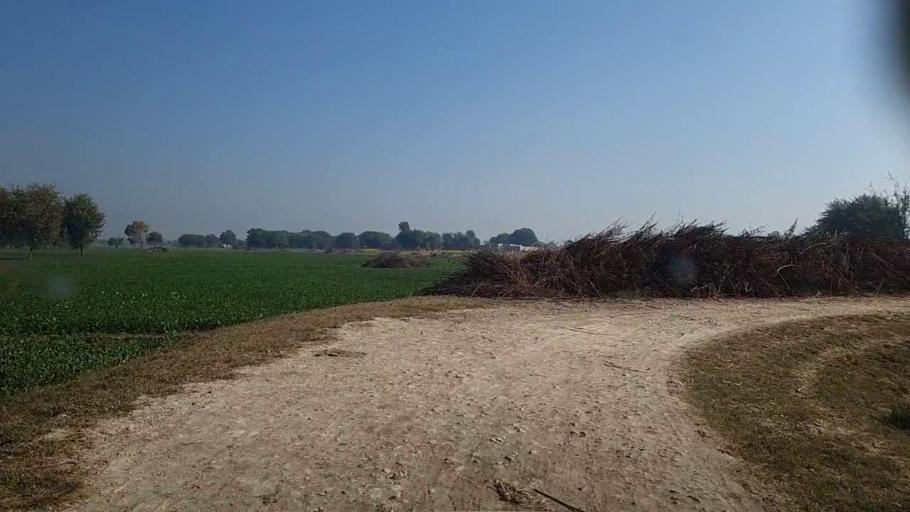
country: PK
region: Sindh
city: Khairpur
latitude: 27.9432
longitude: 69.6862
